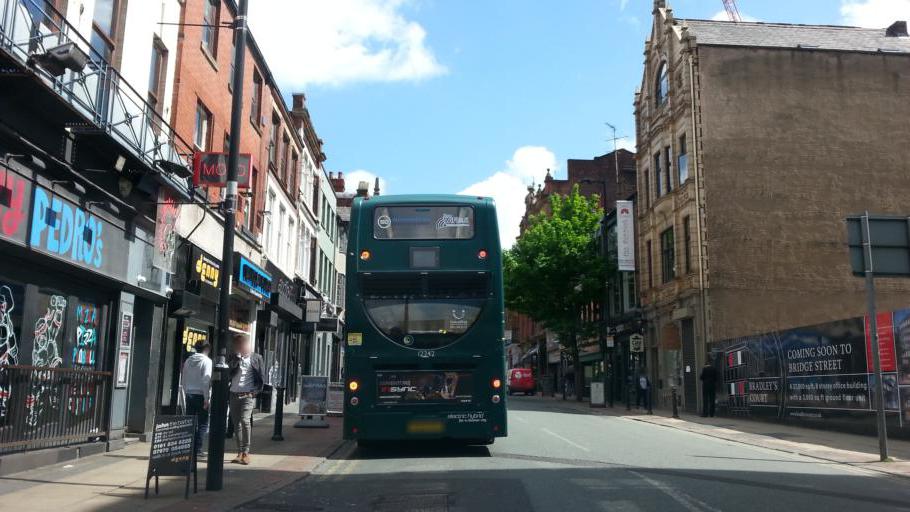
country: GB
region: England
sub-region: Manchester
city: Manchester
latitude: 53.4804
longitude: -2.2500
